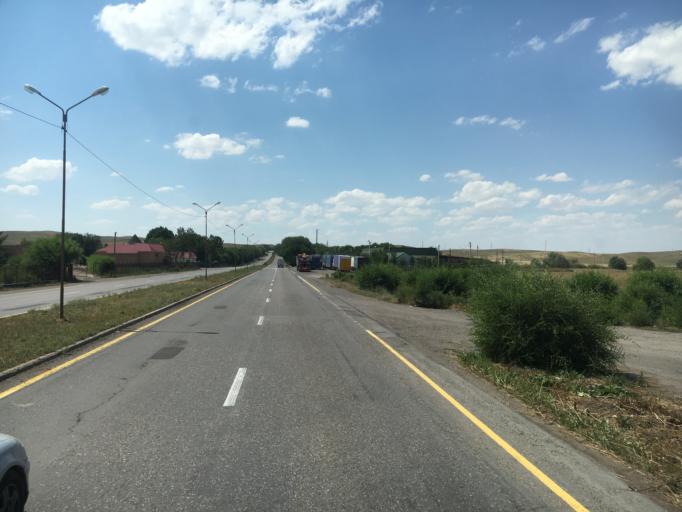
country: KZ
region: Almaty Oblysy
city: Burunday
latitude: 43.2829
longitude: 76.2732
